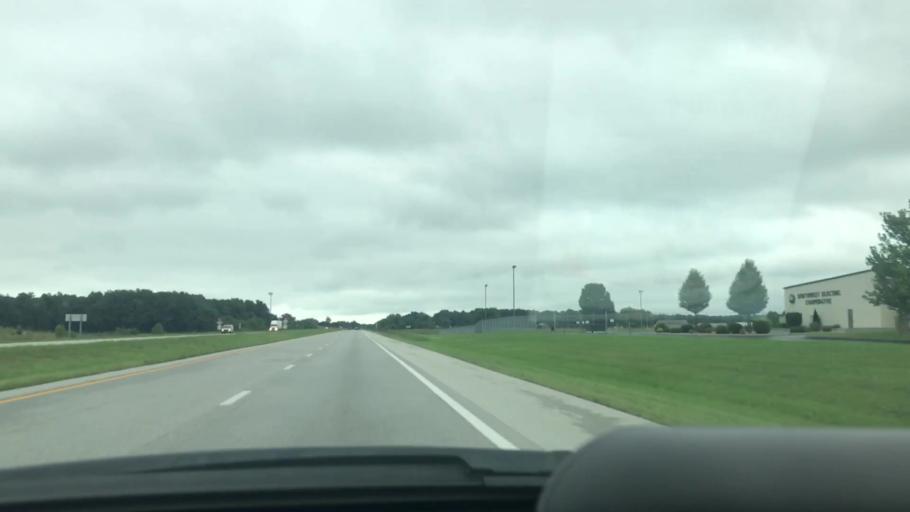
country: US
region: Missouri
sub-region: Greene County
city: Strafford
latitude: 37.2743
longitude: -93.2120
